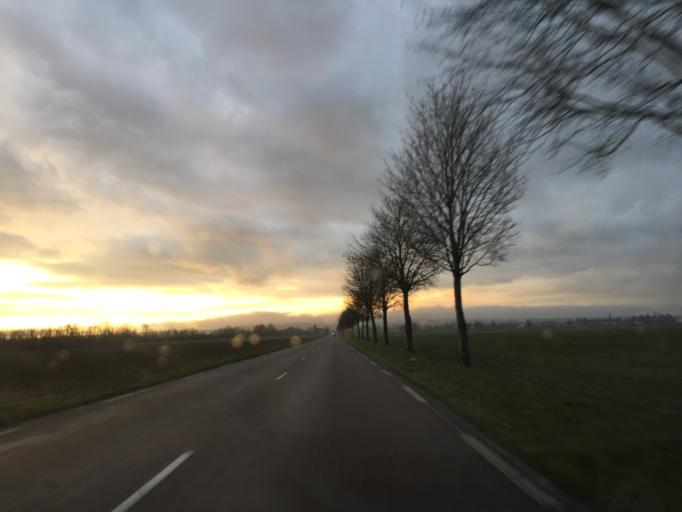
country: FR
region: Franche-Comte
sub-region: Departement du Jura
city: Choisey
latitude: 47.0370
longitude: 5.4954
